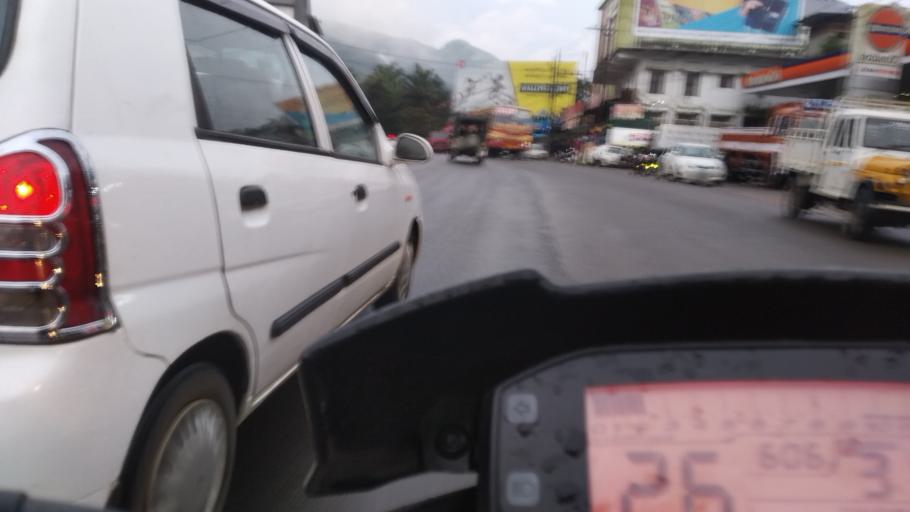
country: IN
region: Kerala
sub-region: Idukki
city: Munnar
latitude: 10.0146
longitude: 76.9503
